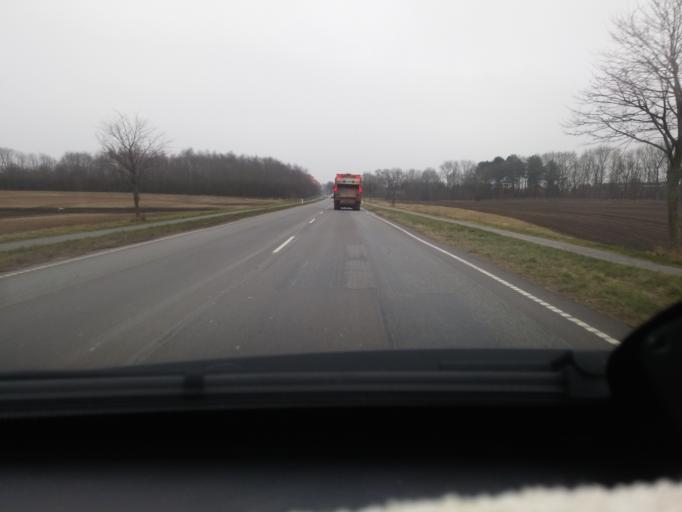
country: DK
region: South Denmark
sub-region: Nyborg Kommune
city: Nyborg
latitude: 55.3221
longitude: 10.7728
